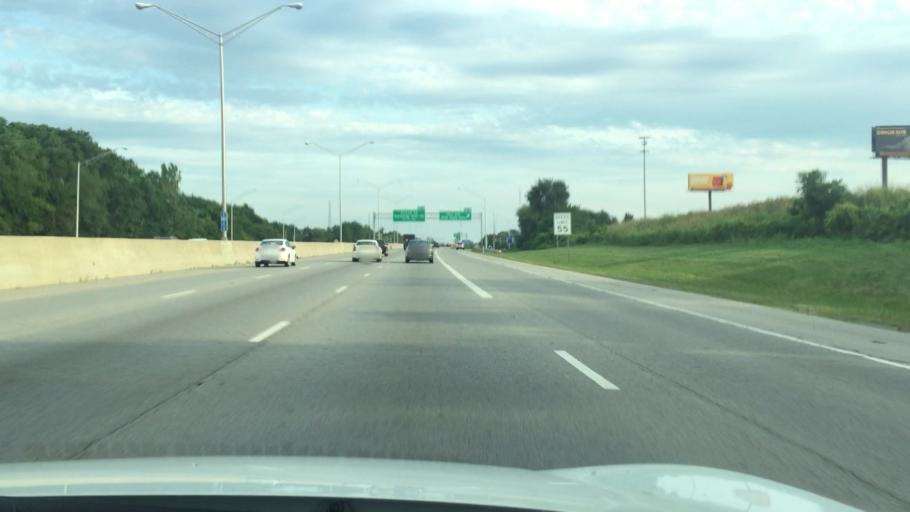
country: US
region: Ohio
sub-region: Franklin County
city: Grandview Heights
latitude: 40.0110
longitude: -83.0320
